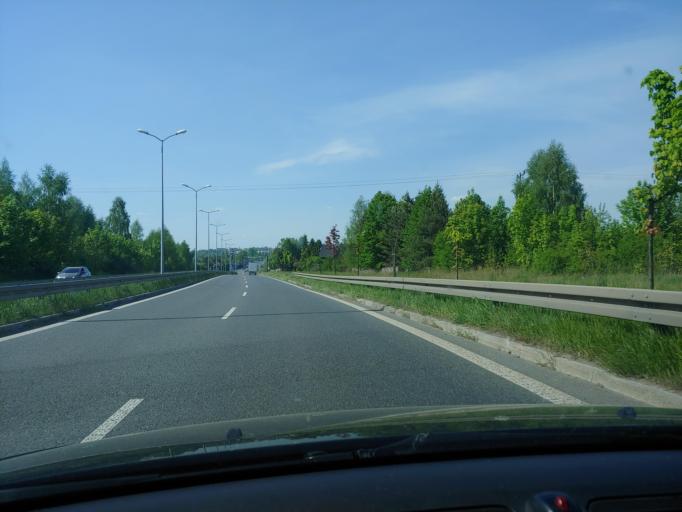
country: PL
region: Silesian Voivodeship
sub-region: Jaworzno
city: Jaworzno
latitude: 50.1771
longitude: 19.2934
